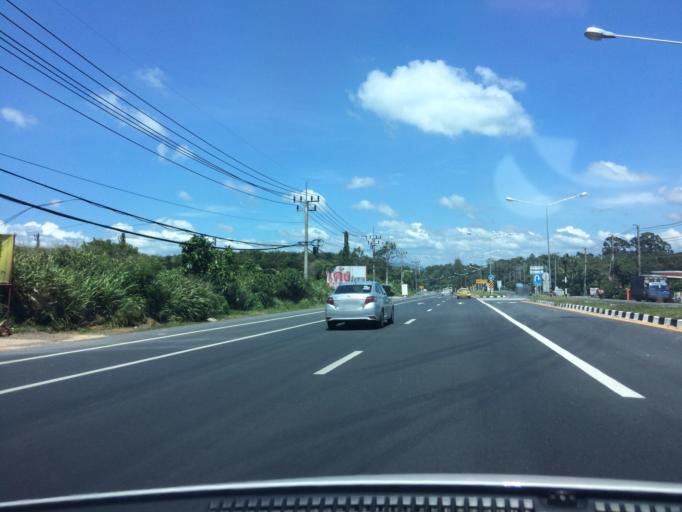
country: TH
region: Phuket
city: Thalang
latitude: 8.1352
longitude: 98.3410
